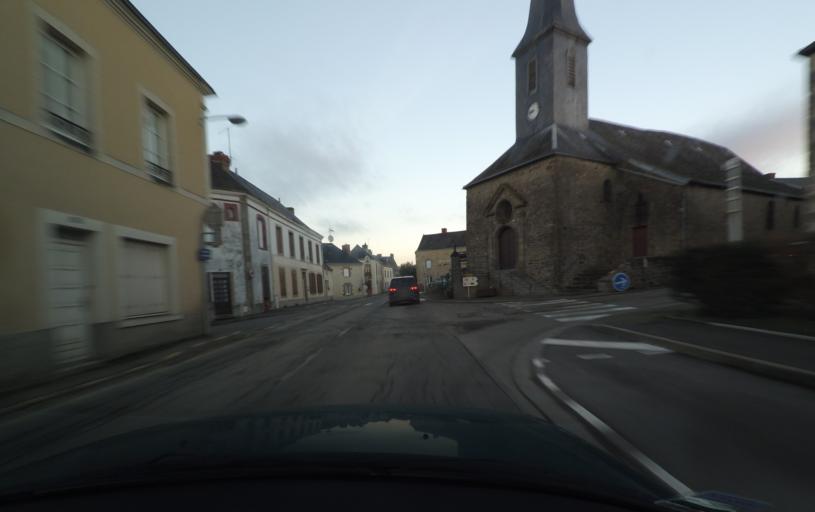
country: FR
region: Pays de la Loire
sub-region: Departement de la Mayenne
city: Evron
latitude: 48.1968
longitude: -0.3742
